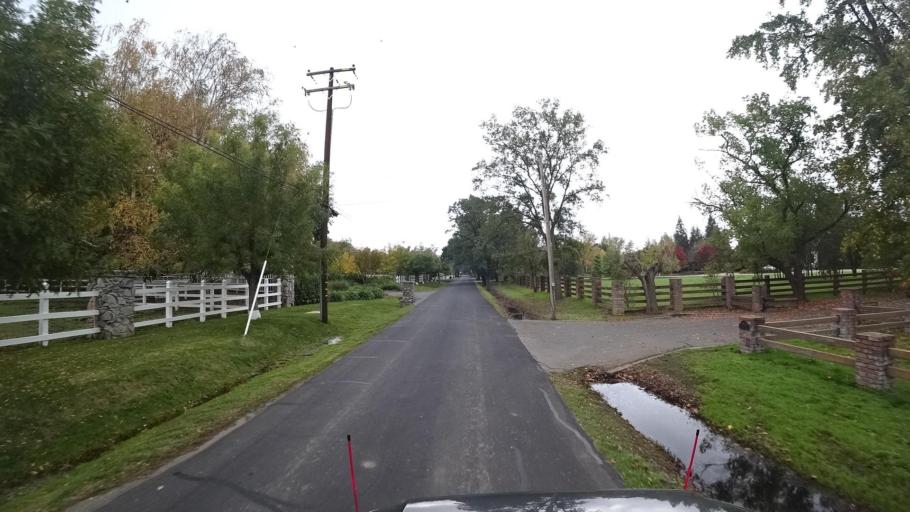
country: US
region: California
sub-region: Sacramento County
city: Wilton
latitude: 38.4337
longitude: -121.3115
